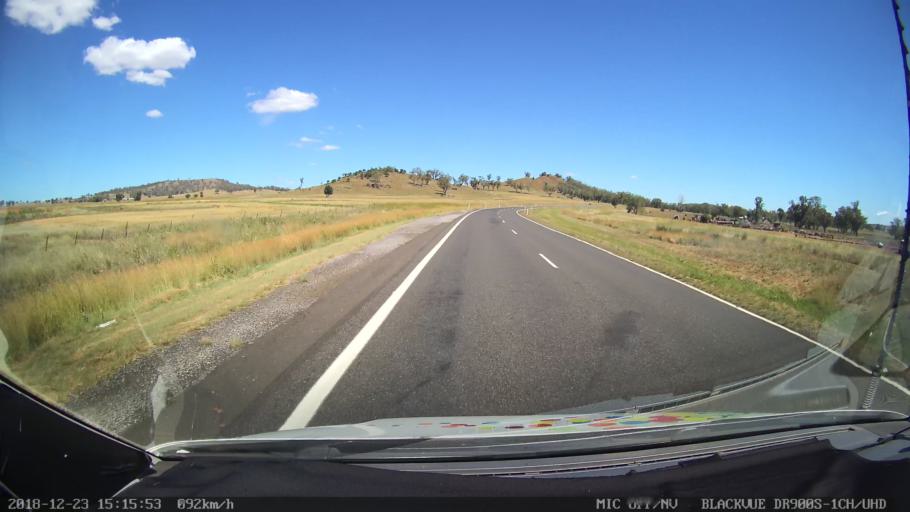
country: AU
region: New South Wales
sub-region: Tamworth Municipality
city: Manilla
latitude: -30.7920
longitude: 150.7454
